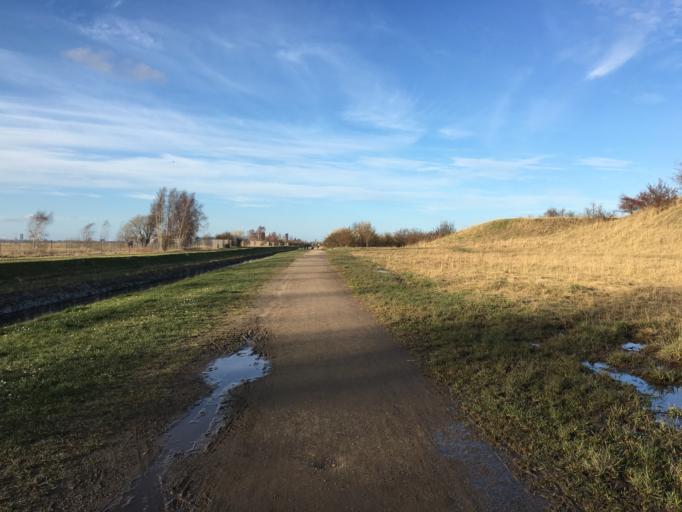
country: DK
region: Capital Region
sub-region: Tarnby Kommune
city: Tarnby
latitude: 55.5925
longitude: 12.5719
